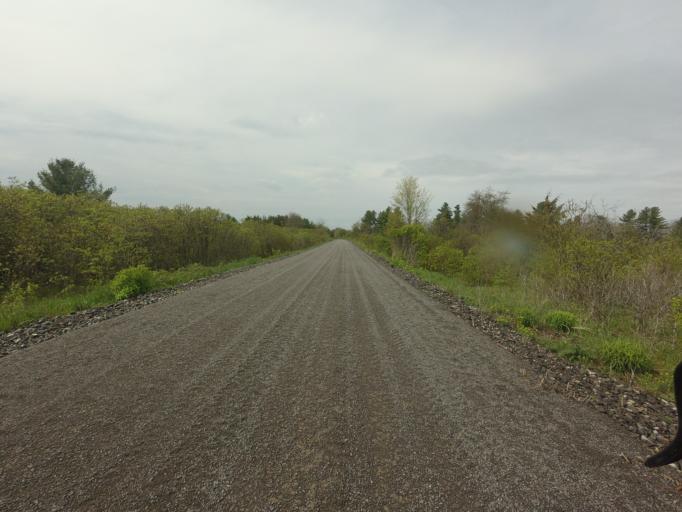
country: CA
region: Ontario
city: Carleton Place
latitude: 45.1571
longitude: -76.1448
